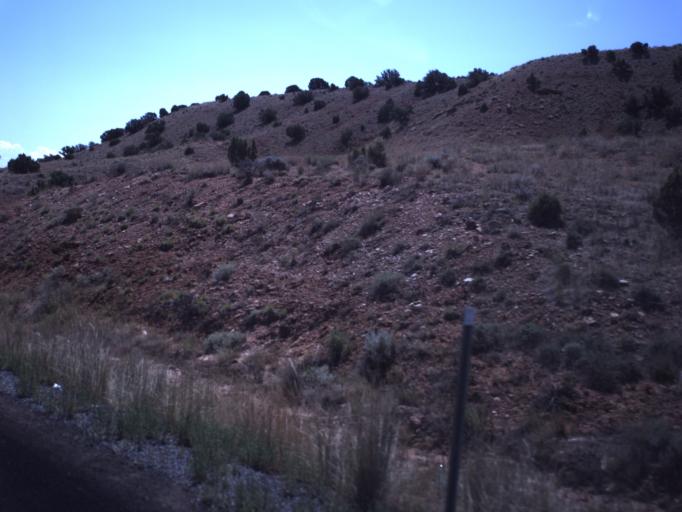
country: US
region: Utah
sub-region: Uintah County
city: Maeser
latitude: 40.4099
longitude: -109.7083
